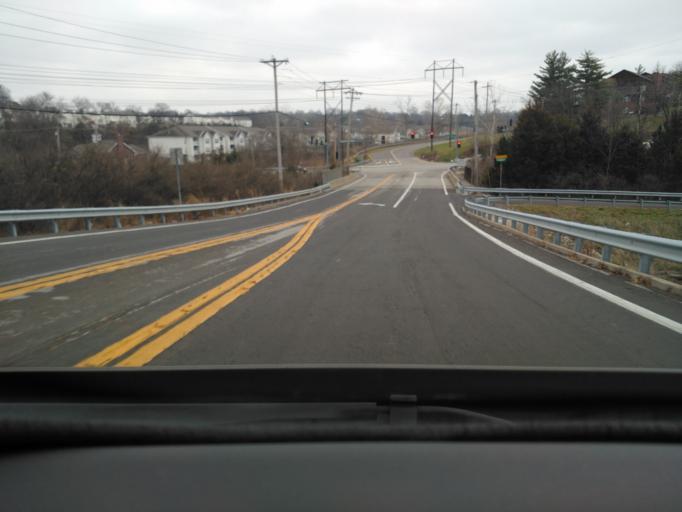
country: US
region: Missouri
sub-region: Saint Louis County
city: Mehlville
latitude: 38.4950
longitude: -90.3458
